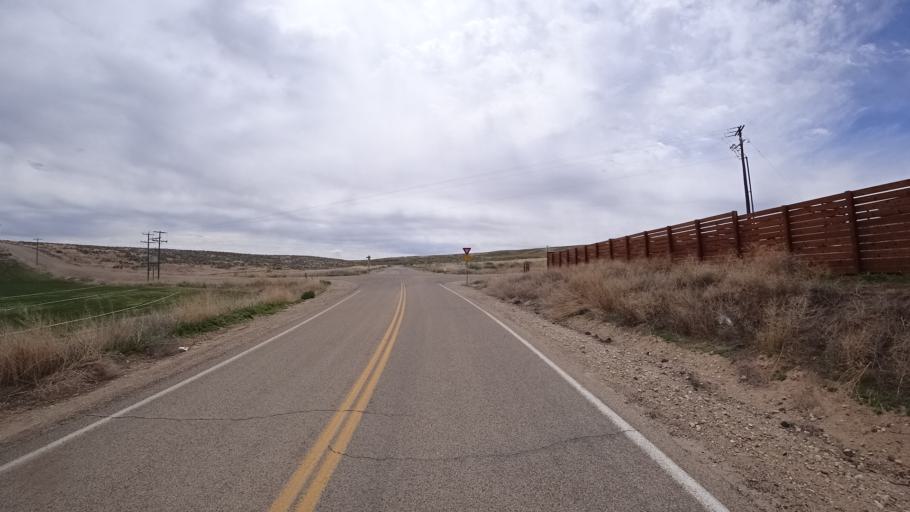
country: US
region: Idaho
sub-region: Ada County
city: Kuna
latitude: 43.4598
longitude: -116.4435
